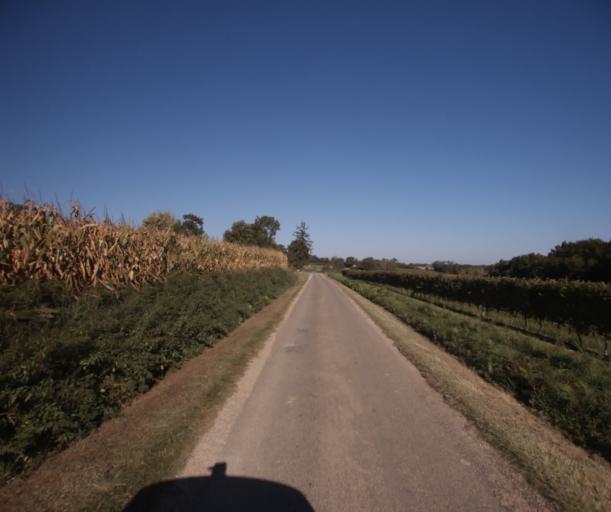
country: FR
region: Midi-Pyrenees
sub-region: Departement du Gers
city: Cazaubon
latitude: 43.9109
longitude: 0.0047
